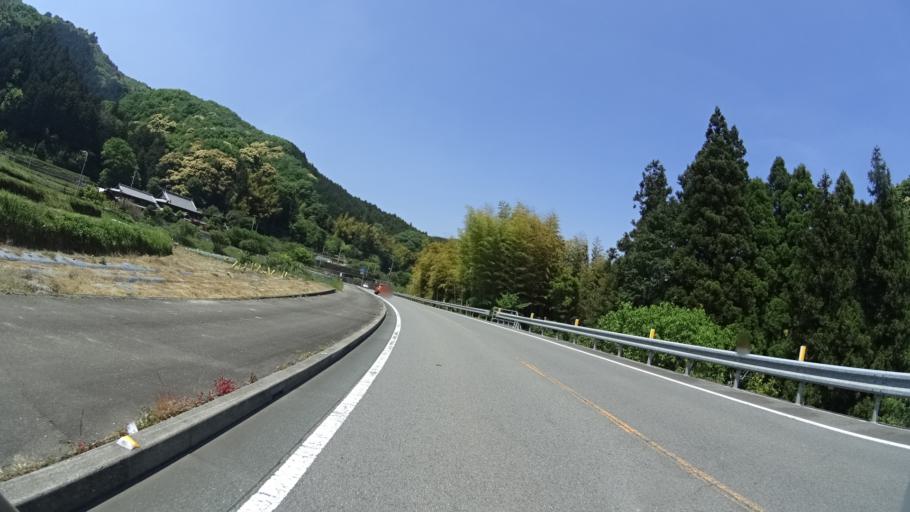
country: JP
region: Ehime
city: Hojo
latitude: 33.9783
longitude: 132.9047
